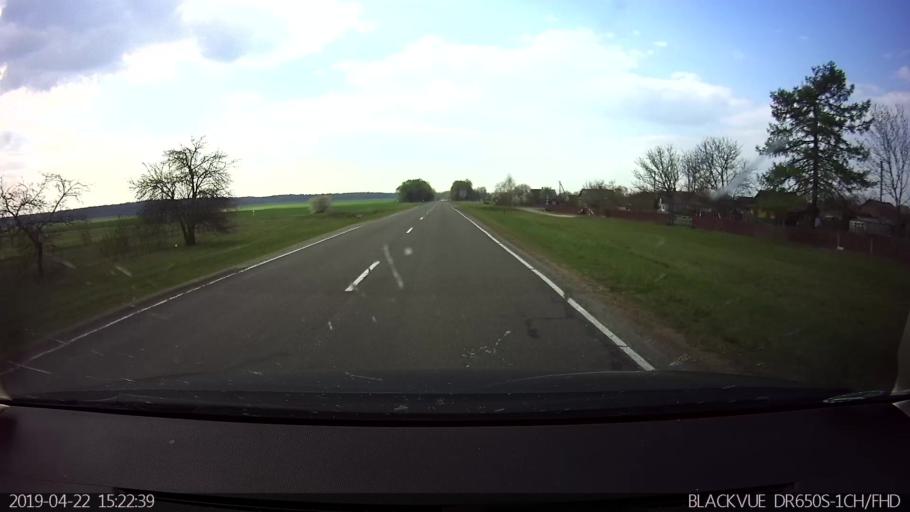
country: BY
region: Brest
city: Vysokaye
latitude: 52.3510
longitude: 23.4417
